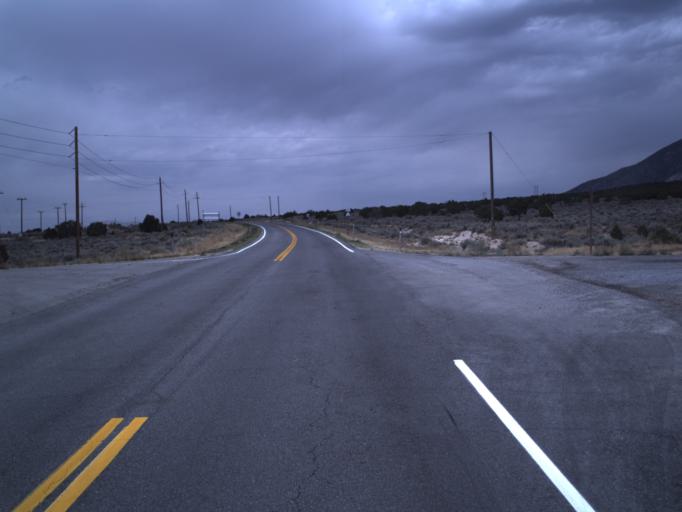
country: US
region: Utah
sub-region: Tooele County
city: Tooele
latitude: 40.3244
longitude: -112.2882
